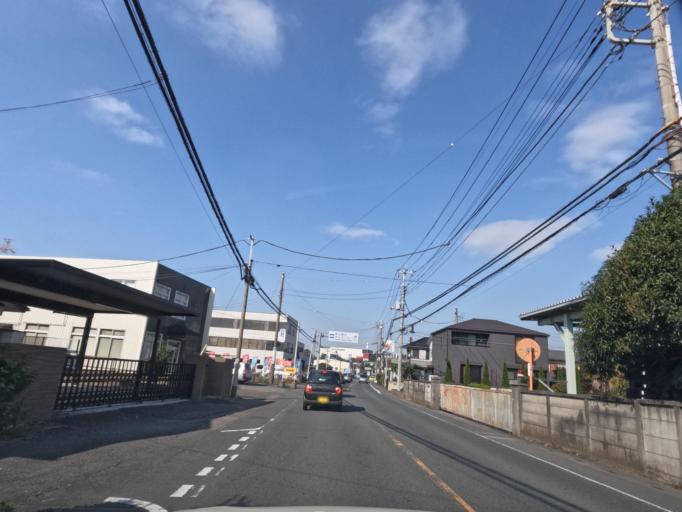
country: JP
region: Saitama
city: Ageoshimo
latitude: 35.9810
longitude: 139.6107
